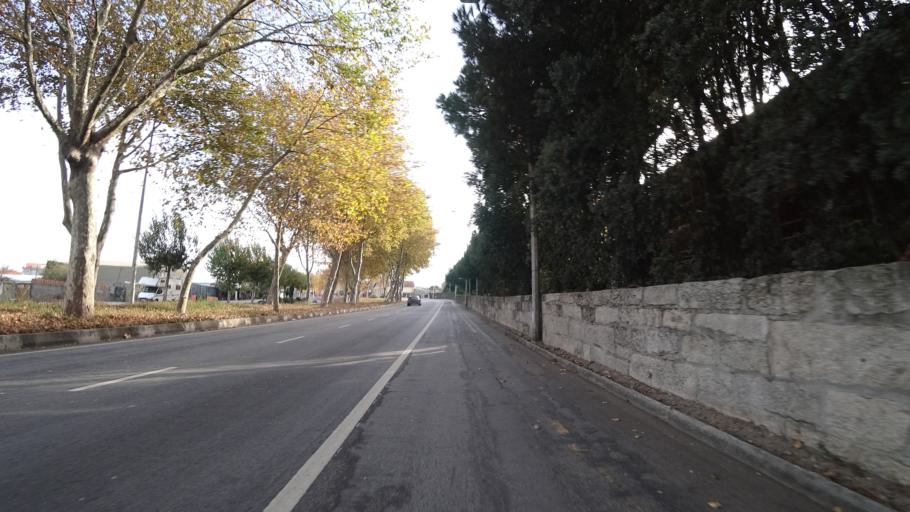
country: PT
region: Porto
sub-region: Matosinhos
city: Matosinhos
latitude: 41.1717
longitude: -8.6768
